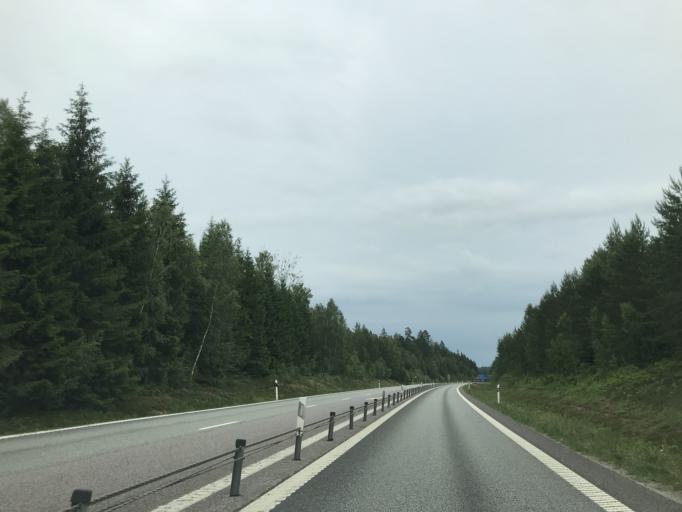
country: SE
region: Skane
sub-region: Hassleholms Kommun
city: Hastveda
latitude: 56.2852
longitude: 13.9948
